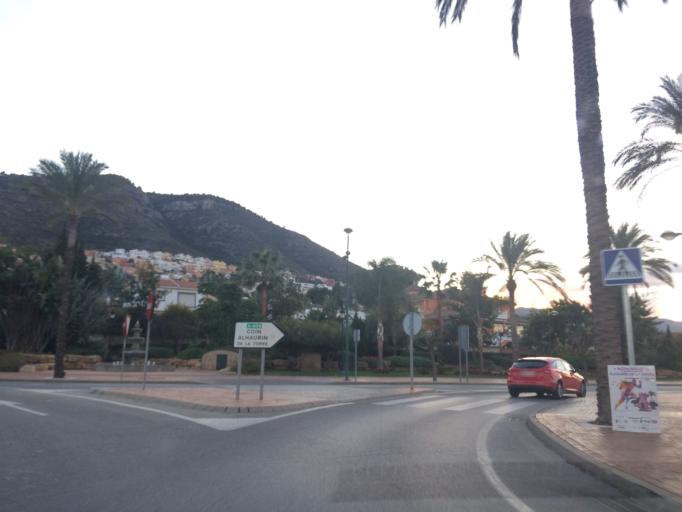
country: ES
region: Andalusia
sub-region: Provincia de Malaga
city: Alhaurin de la Torre
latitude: 36.6608
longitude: -4.5298
